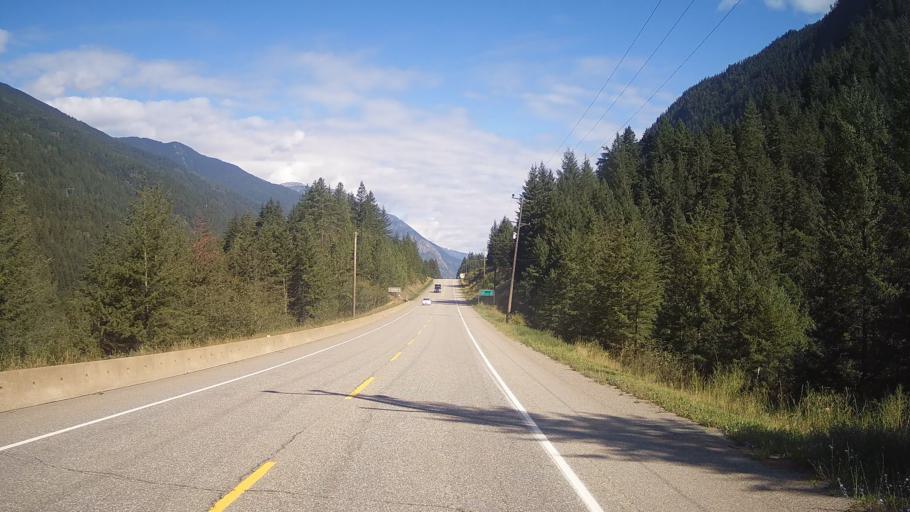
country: CA
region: British Columbia
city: Hope
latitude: 50.0310
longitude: -121.5302
